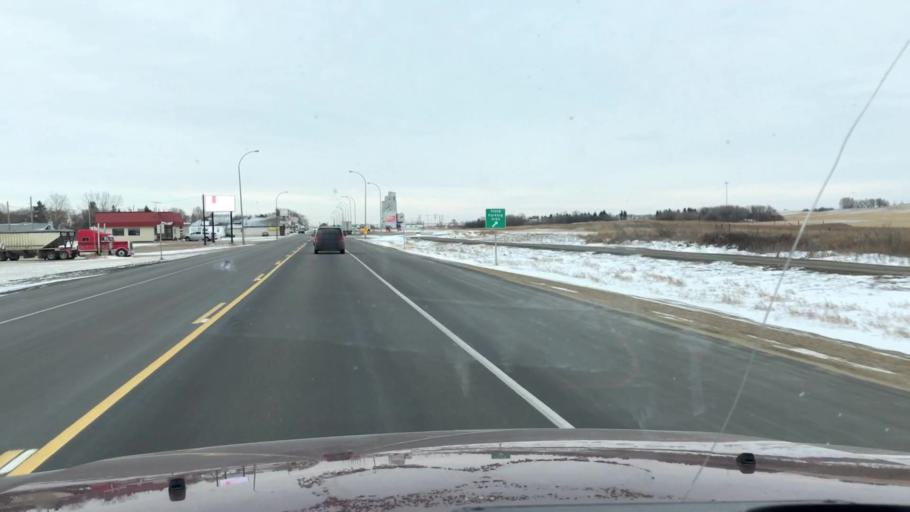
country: CA
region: Saskatchewan
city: Moose Jaw
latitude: 50.8538
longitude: -105.5734
